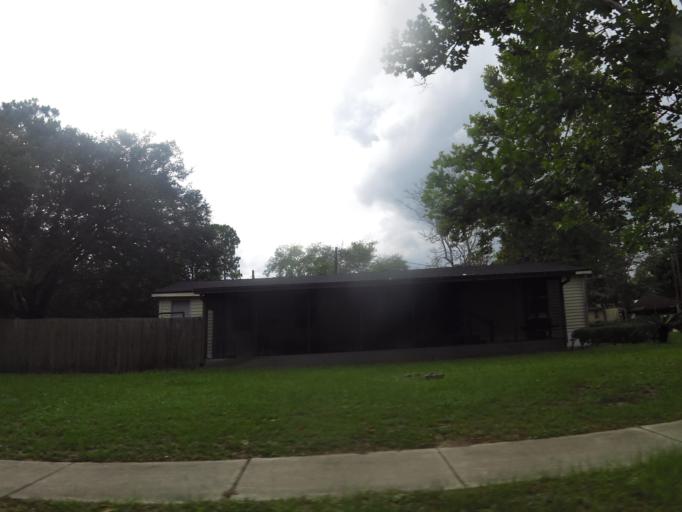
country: US
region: Florida
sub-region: Duval County
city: Jacksonville
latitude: 30.3147
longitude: -81.5318
